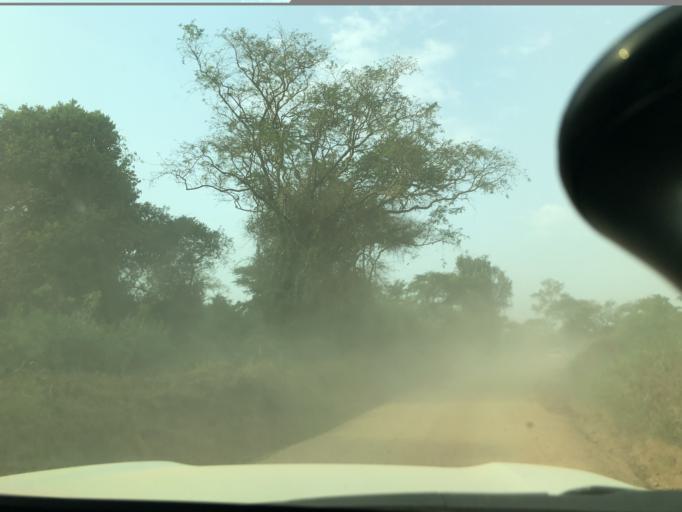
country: UG
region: Western Region
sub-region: Kasese District
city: Margherita
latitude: 0.1929
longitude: 29.6571
